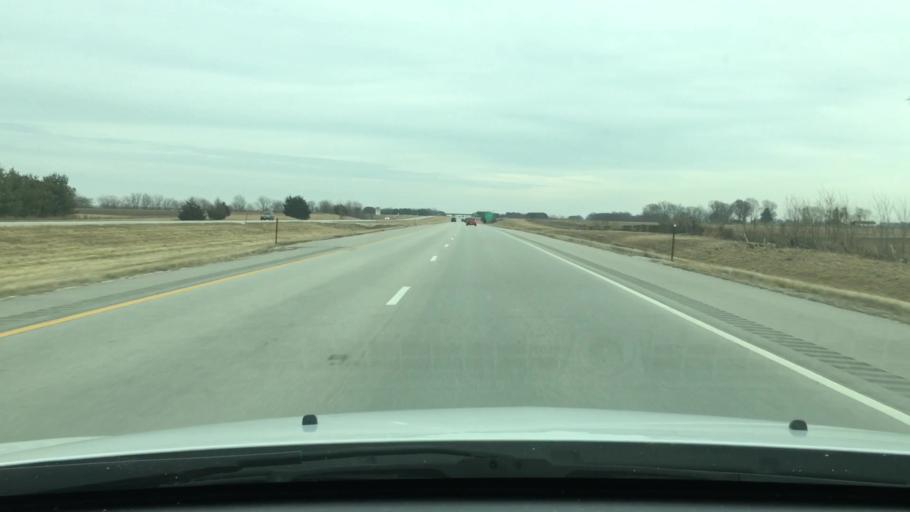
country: US
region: Illinois
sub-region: Sangamon County
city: New Berlin
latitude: 39.7368
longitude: -90.0633
